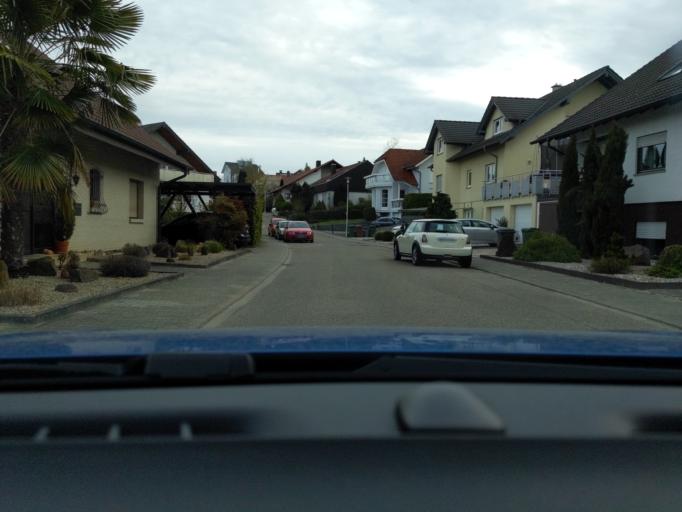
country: DE
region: Baden-Wuerttemberg
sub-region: Karlsruhe Region
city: Dielheim
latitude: 49.2881
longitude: 8.7370
